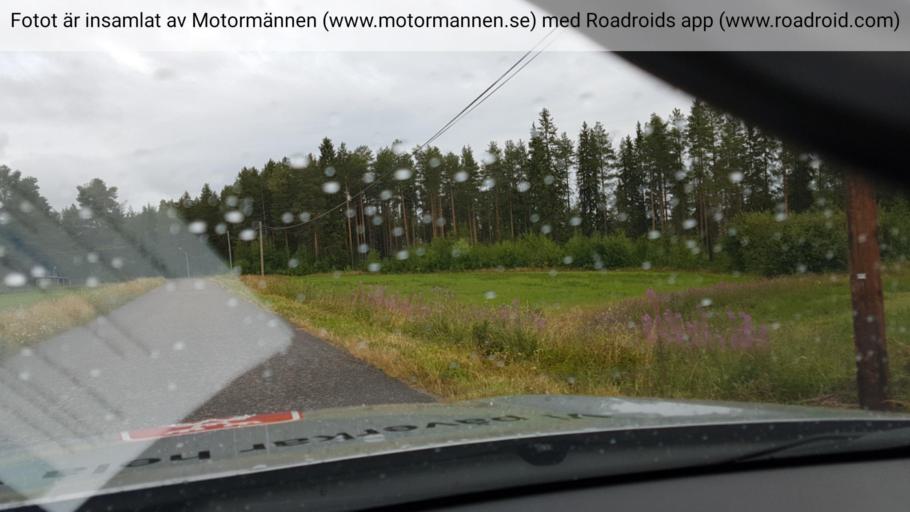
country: SE
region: Norrbotten
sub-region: Alvsbyns Kommun
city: AElvsbyn
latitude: 66.0672
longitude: 20.9410
